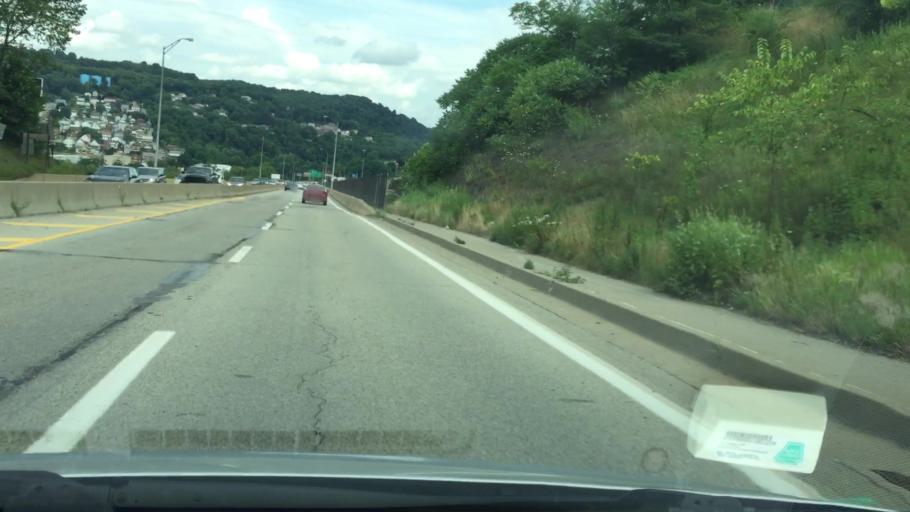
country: US
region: Pennsylvania
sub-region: Allegheny County
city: Tarentum
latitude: 40.5946
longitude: -79.7532
